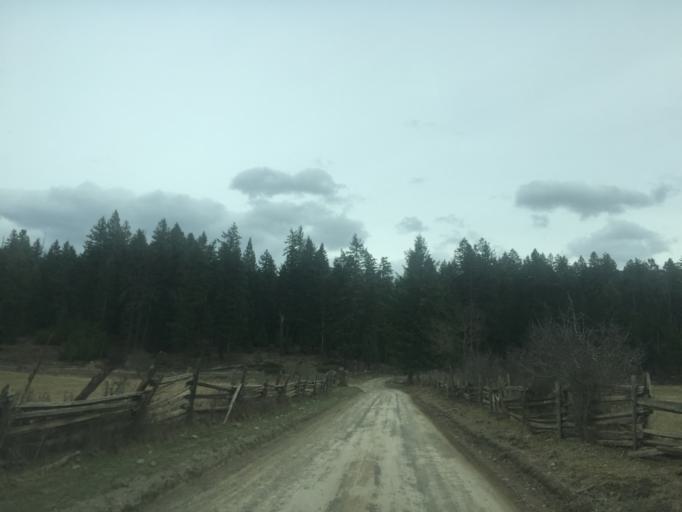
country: CA
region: British Columbia
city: Kamloops
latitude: 51.3616
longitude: -120.1557
